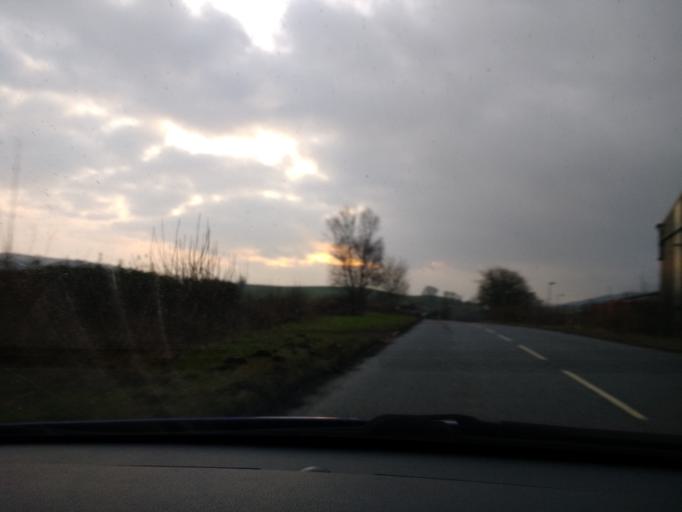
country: GB
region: England
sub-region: Cumbria
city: Milnthorpe
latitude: 54.2442
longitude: -2.7142
